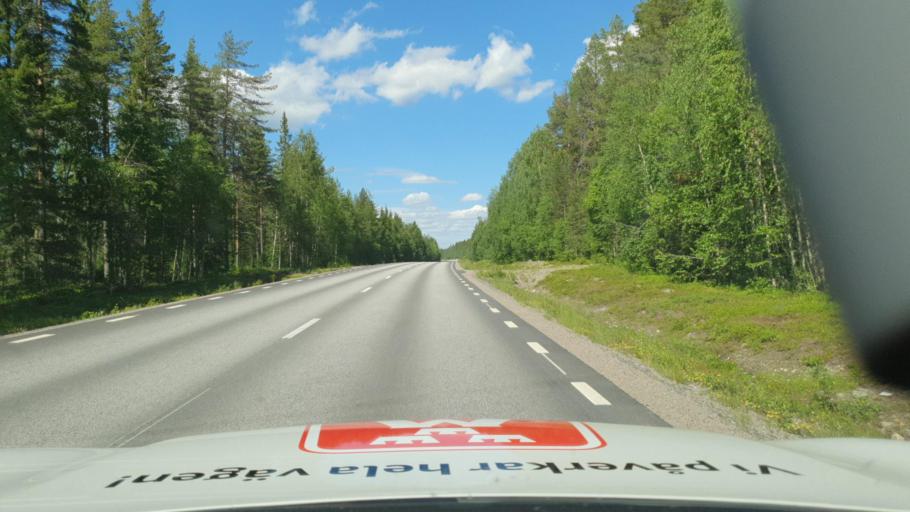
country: SE
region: Vaesterbotten
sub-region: Skelleftea Kommun
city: Boliden
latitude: 64.9088
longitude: 20.3455
